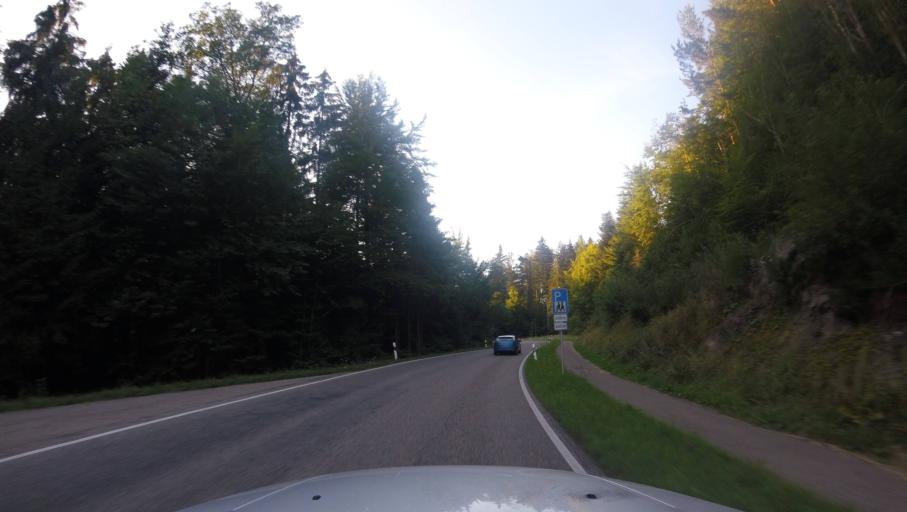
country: DE
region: Baden-Wuerttemberg
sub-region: Regierungsbezirk Stuttgart
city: Kaisersbach
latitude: 48.9171
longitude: 9.6677
